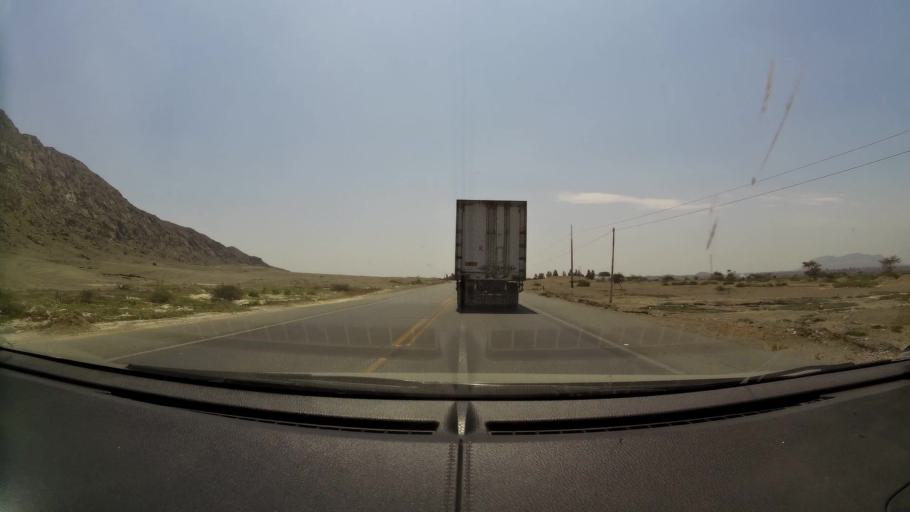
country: PE
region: La Libertad
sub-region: Provincia de Pacasmayo
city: Guadalupe
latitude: -7.2826
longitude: -79.4741
